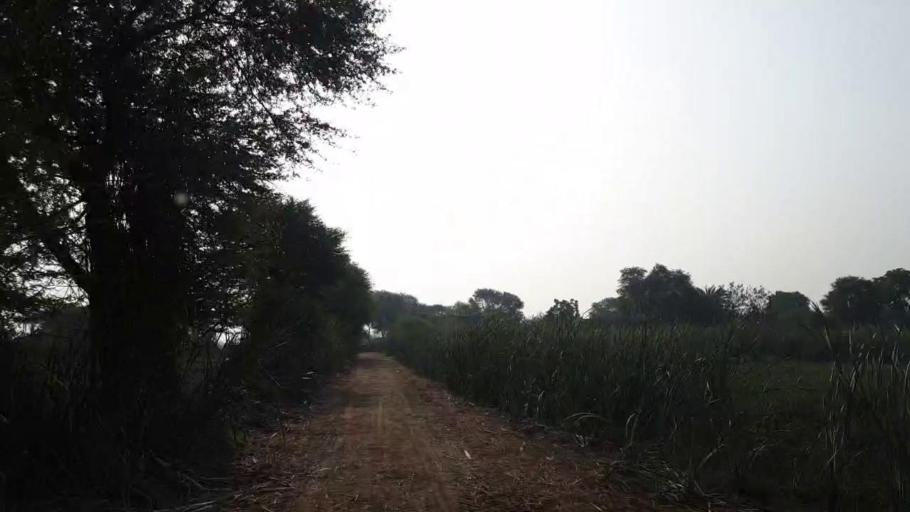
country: PK
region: Sindh
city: Matli
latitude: 25.0676
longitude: 68.6085
